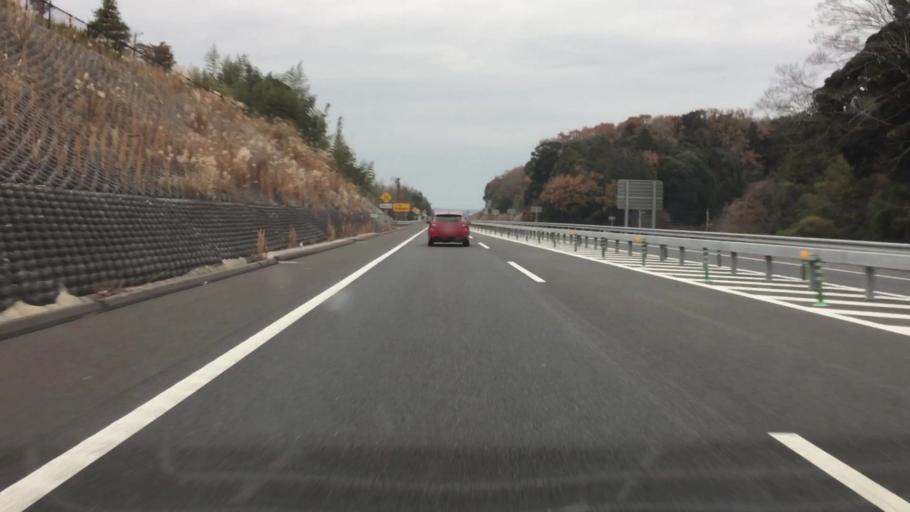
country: JP
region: Ibaraki
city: Edosaki
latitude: 35.8718
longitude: 140.3889
